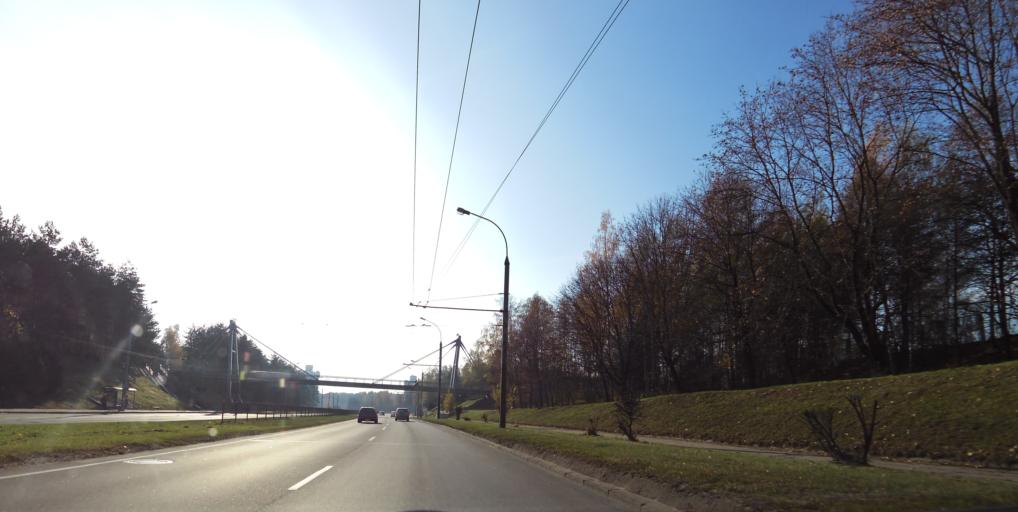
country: LT
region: Vilnius County
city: Lazdynai
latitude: 54.6859
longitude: 25.2074
